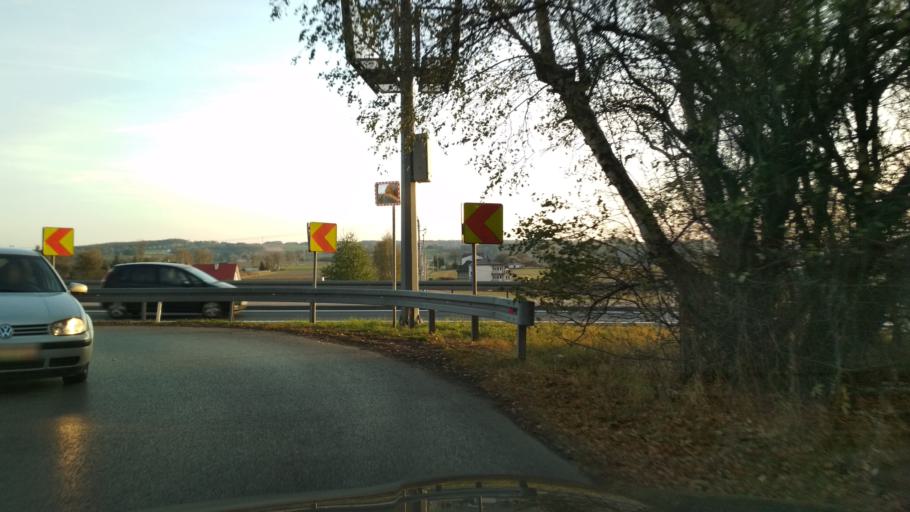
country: PL
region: Subcarpathian Voivodeship
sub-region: Powiat ropczycko-sedziszowski
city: Sedziszow Malopolski
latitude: 50.0626
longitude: 21.7117
